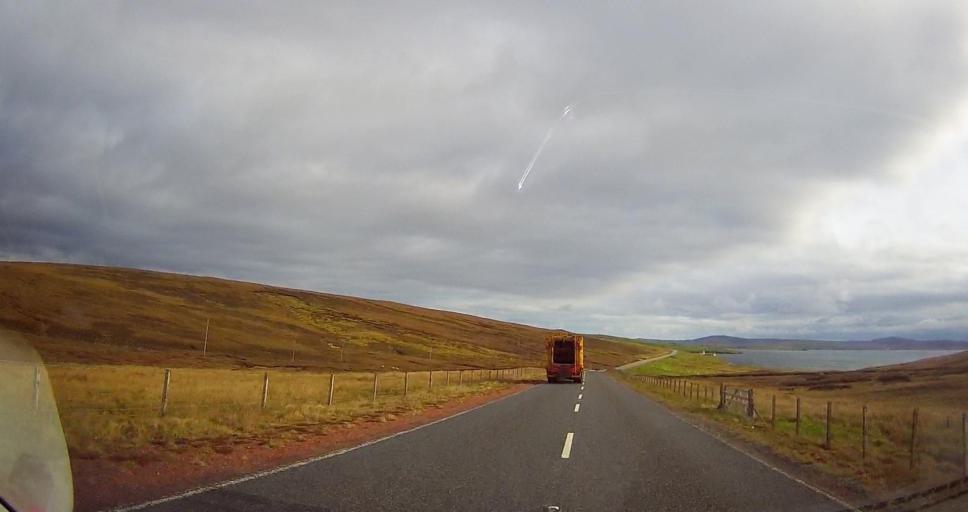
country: GB
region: Scotland
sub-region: Shetland Islands
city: Lerwick
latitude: 60.4506
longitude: -1.2127
